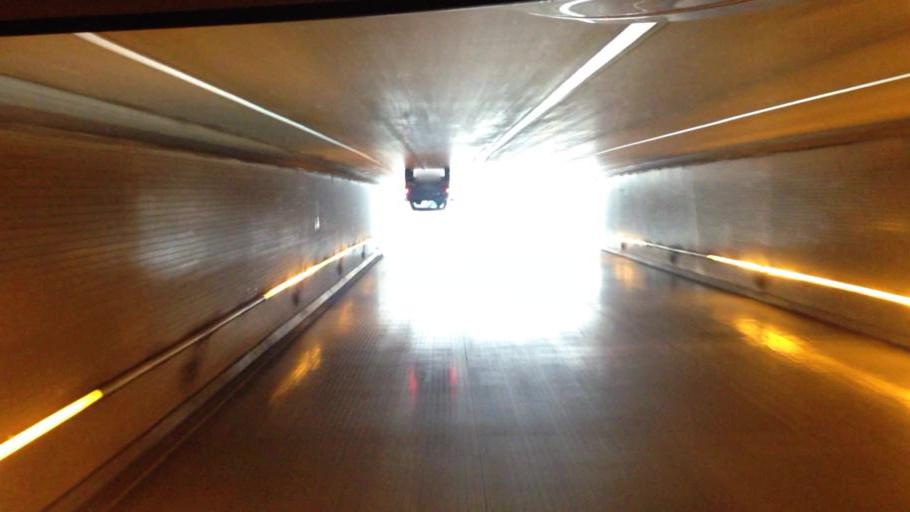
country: US
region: Minnesota
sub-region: Hennepin County
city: Minneapolis
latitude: 44.9686
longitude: -93.2876
